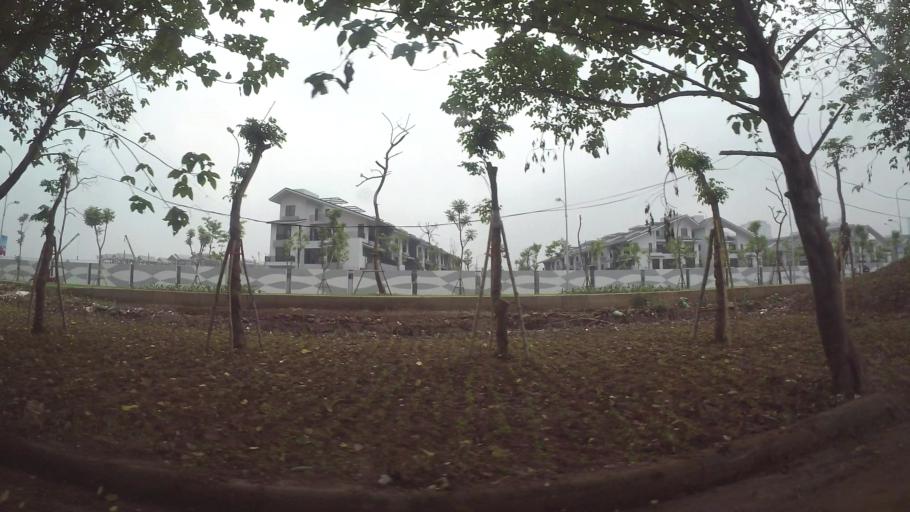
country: VN
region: Ha Noi
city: Van Dien
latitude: 20.9740
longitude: 105.8708
